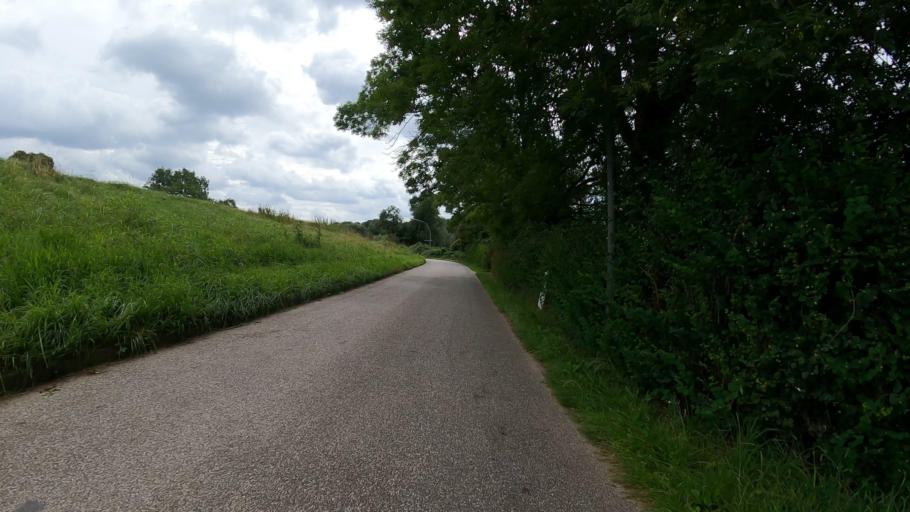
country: DE
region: Lower Saxony
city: Neu Wulmstorf
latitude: 53.5204
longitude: 9.8451
